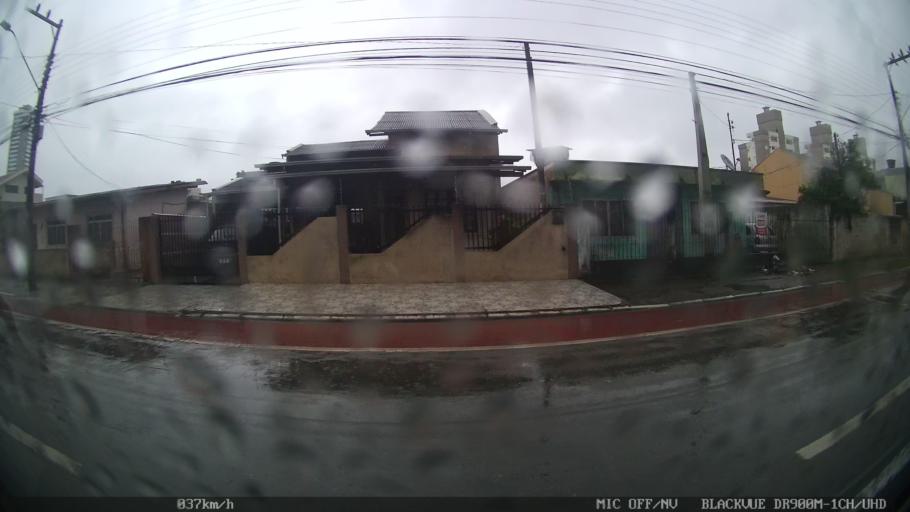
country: BR
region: Santa Catarina
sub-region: Itajai
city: Itajai
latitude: -26.9103
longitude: -48.6794
